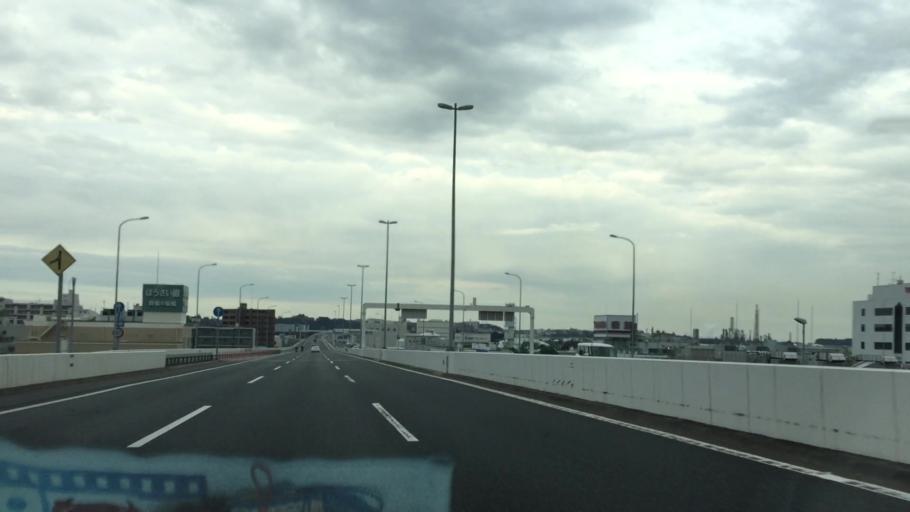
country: JP
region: Kanagawa
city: Yokohama
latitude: 35.3997
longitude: 139.6188
